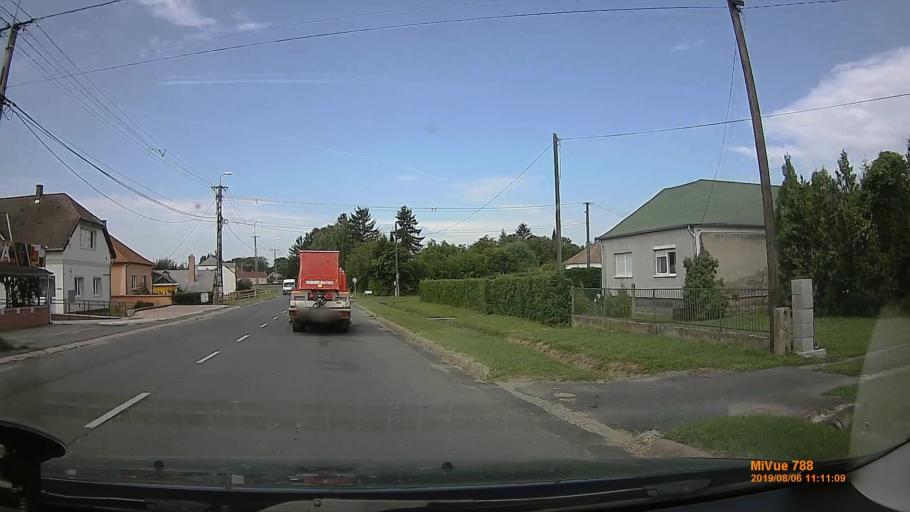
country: HU
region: Zala
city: Becsehely
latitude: 46.4476
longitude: 16.7846
